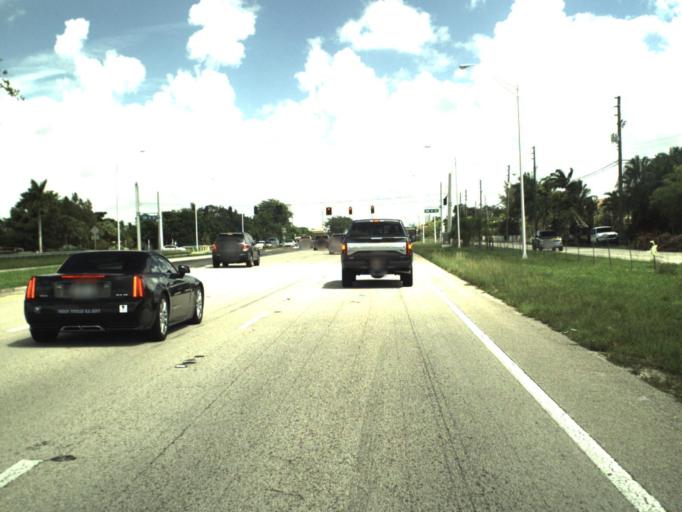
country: US
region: Florida
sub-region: Broward County
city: Pine Island Ridge
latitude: 26.1080
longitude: -80.3136
